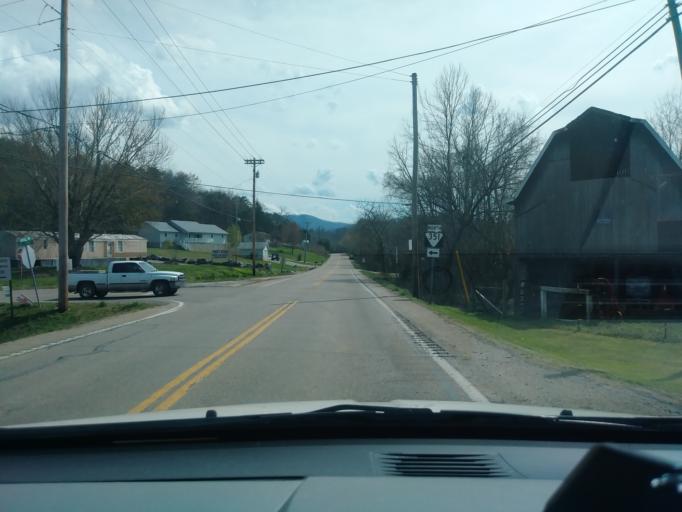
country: US
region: Tennessee
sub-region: Greene County
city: Greeneville
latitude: 36.0432
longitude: -82.8564
